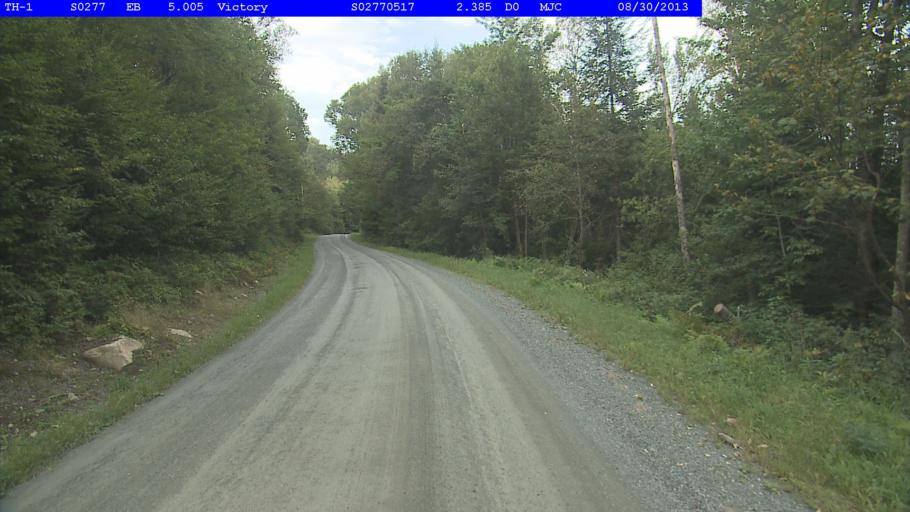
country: US
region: Vermont
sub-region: Caledonia County
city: Lyndonville
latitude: 44.5193
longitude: -71.8218
